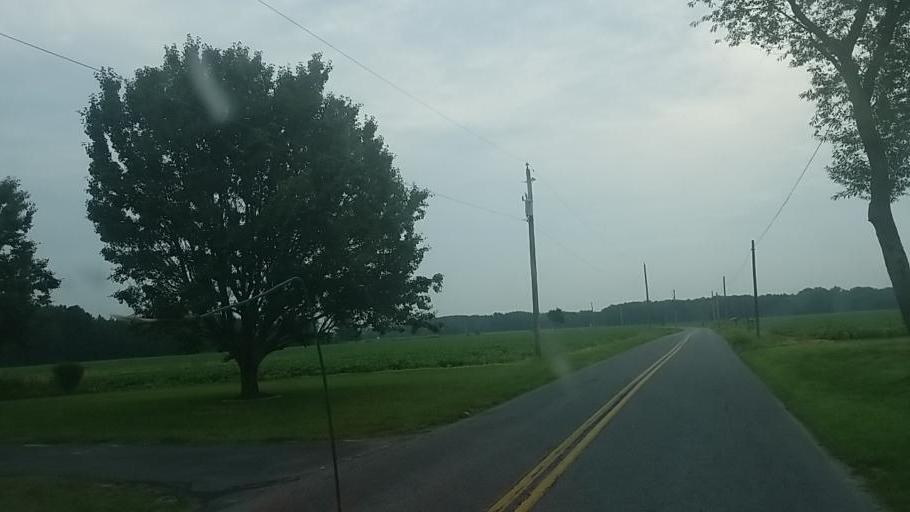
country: US
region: Delaware
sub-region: Sussex County
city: Selbyville
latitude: 38.4479
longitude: -75.2217
